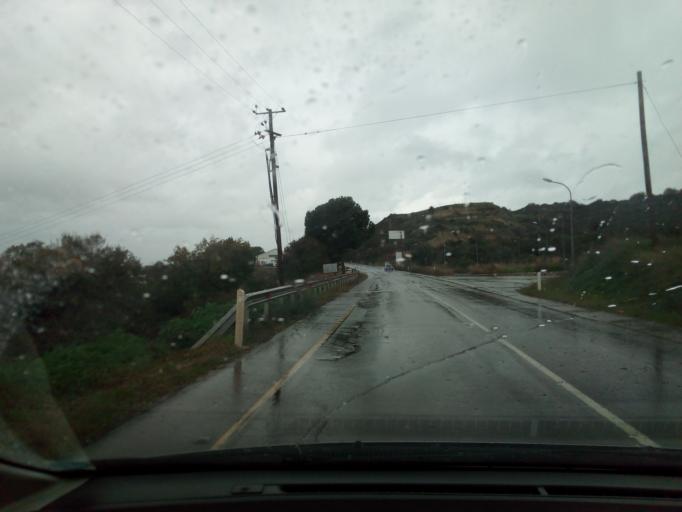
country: CY
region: Pafos
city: Polis
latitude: 34.9892
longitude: 32.4510
